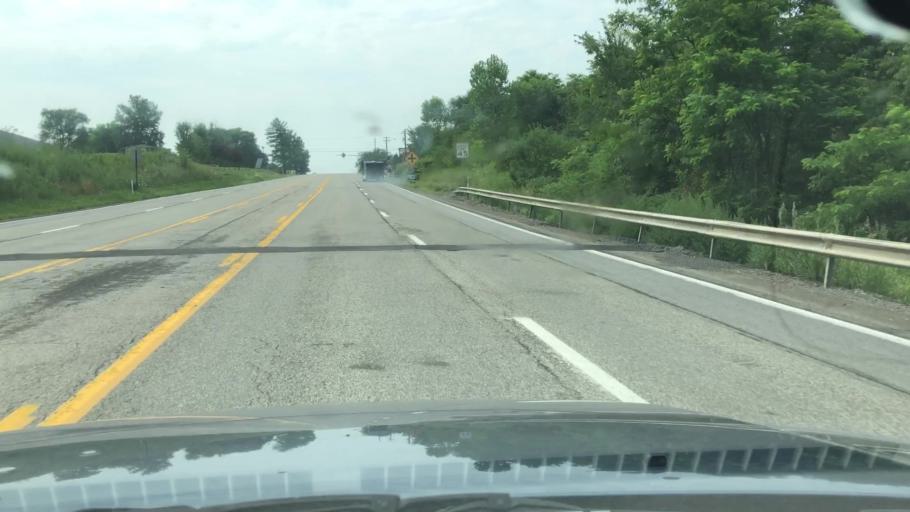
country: US
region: Pennsylvania
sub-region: Butler County
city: Nixon
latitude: 40.7331
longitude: -79.9245
